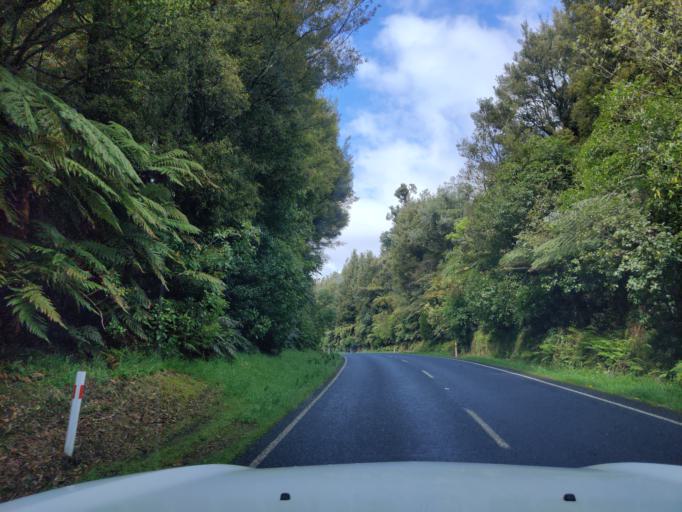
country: NZ
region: Bay of Plenty
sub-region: Rotorua District
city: Rotorua
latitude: -38.1785
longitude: 176.3260
